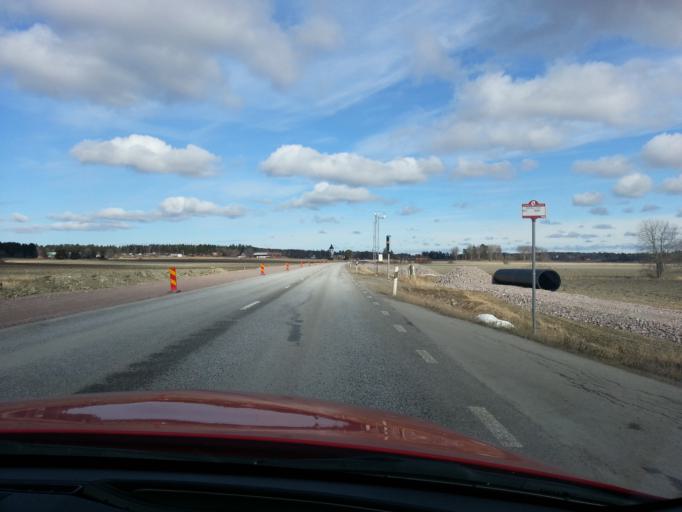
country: SE
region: Uppsala
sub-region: Osthammars Kommun
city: Gimo
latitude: 60.0510
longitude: 18.0532
